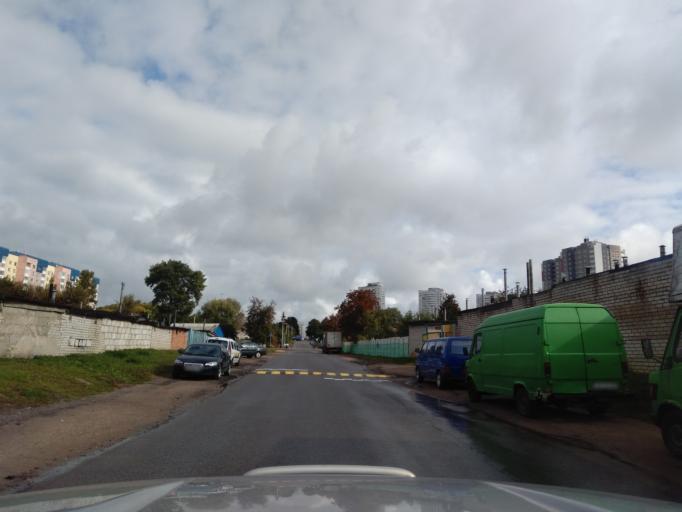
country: BY
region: Minsk
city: Novoye Medvezhino
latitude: 53.9034
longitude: 27.4213
